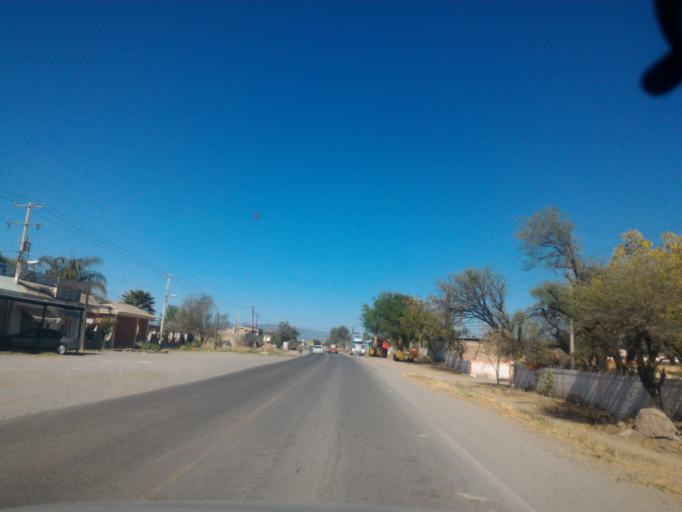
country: MX
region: Guanajuato
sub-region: Leon
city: Malagana (San Antonio del Monte)
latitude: 21.0464
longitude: -101.7577
